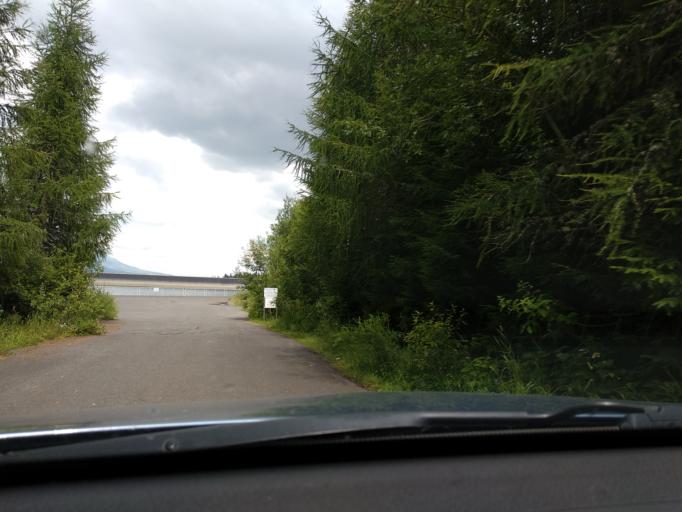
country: SK
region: Zilinsky
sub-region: Okres Liptovsky Mikulas
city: Hybe
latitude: 49.0197
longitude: 19.9066
